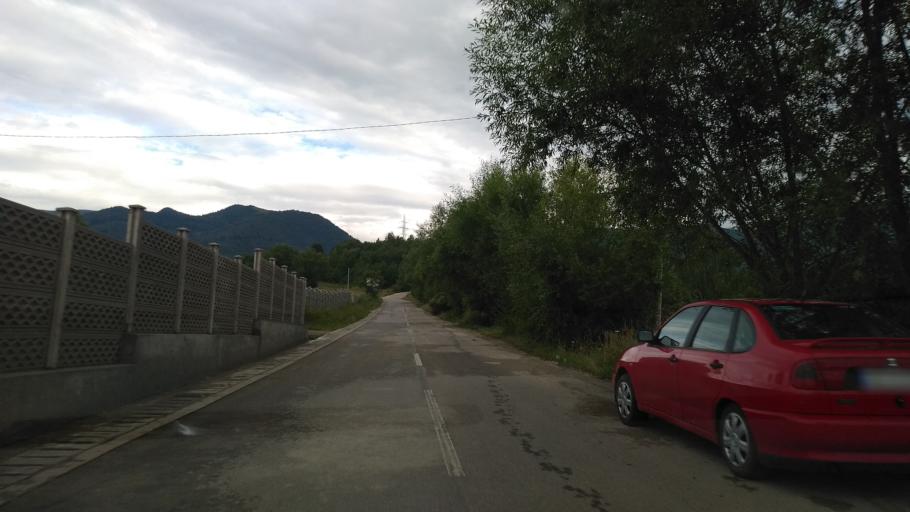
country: RO
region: Hunedoara
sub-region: Municipiul  Vulcan
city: Jiu-Paroseni
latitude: 45.3666
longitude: 23.2835
